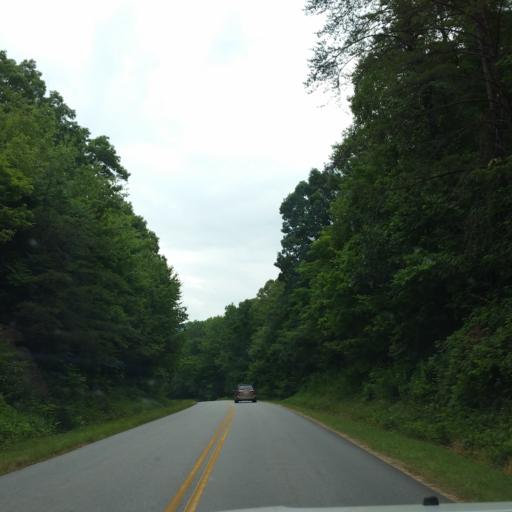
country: US
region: North Carolina
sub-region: Buncombe County
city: Biltmore Forest
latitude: 35.5633
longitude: -82.4901
